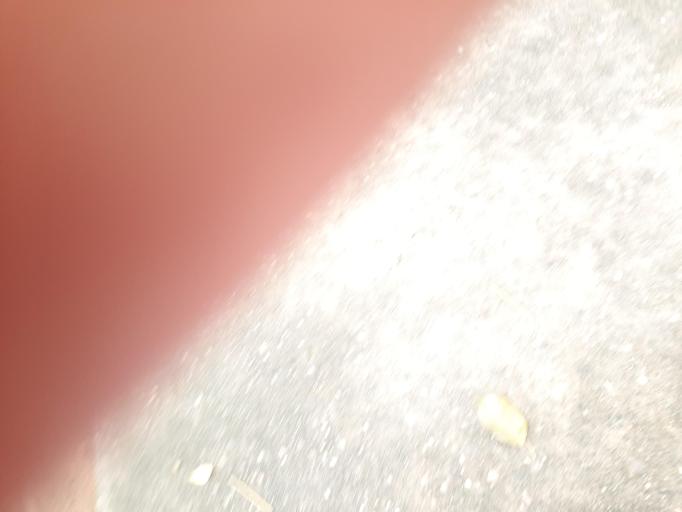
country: MX
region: Jalisco
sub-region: Puerto Vallarta
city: Puerto Vallarta
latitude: 20.6583
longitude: -105.2087
